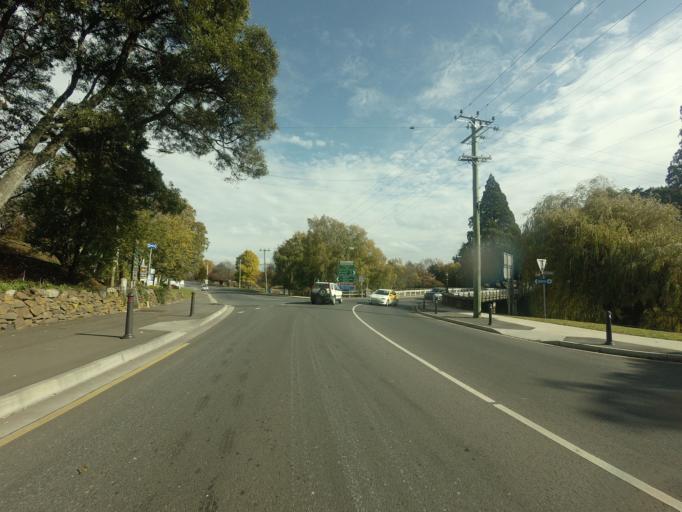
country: AU
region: Tasmania
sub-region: Meander Valley
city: Deloraine
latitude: -41.5247
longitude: 146.6592
